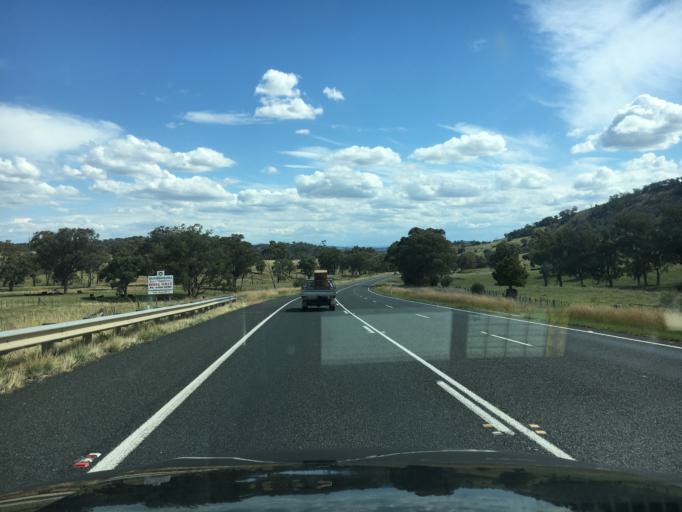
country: AU
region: New South Wales
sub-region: Liverpool Plains
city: Quirindi
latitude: -31.5076
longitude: 150.8603
